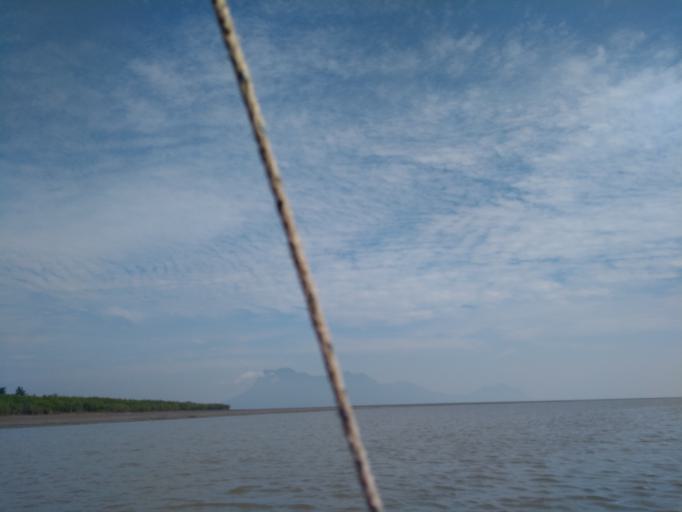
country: MY
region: Sarawak
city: Kuching
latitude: 1.6794
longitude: 110.4247
